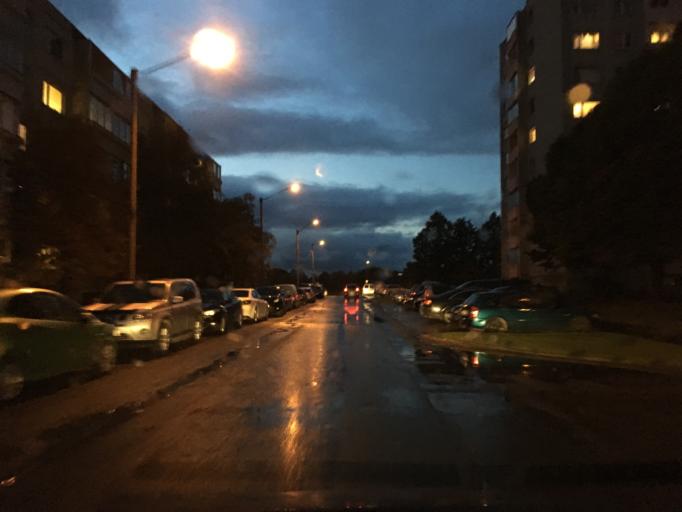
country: EE
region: Harju
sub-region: Tallinna linn
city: Kose
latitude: 59.4424
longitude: 24.8322
